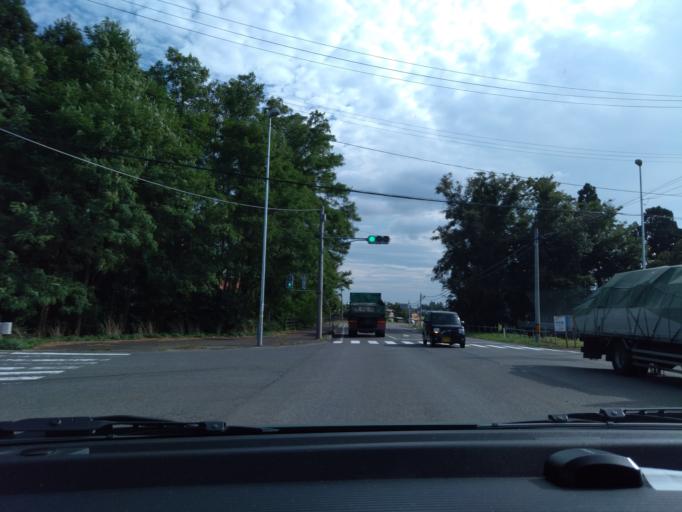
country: JP
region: Iwate
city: Hanamaki
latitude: 39.4605
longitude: 141.1014
